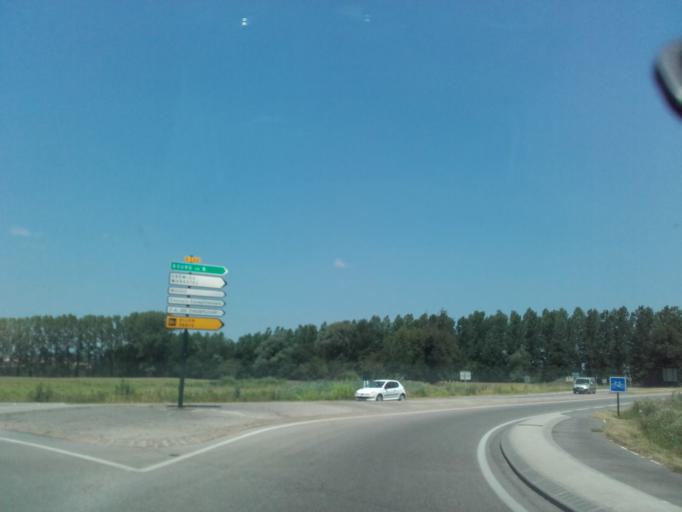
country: FR
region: Rhone-Alpes
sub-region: Departement de l'Isere
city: L'Isle-d'Abeau
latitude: 45.6076
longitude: 5.2533
